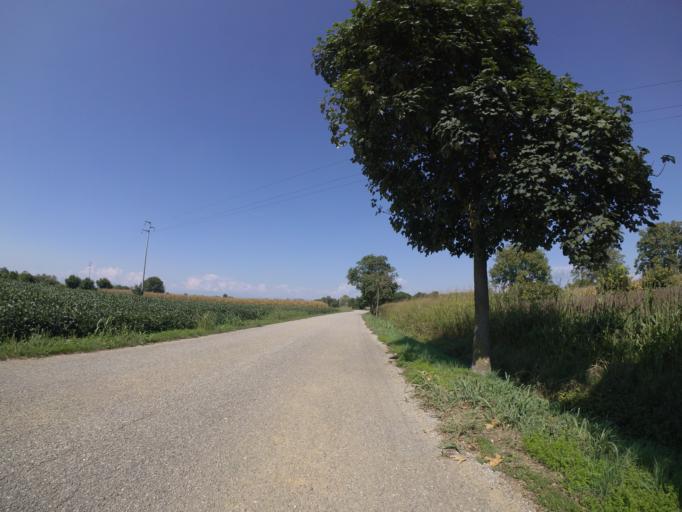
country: IT
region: Friuli Venezia Giulia
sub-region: Provincia di Udine
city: Bertiolo
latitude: 45.9410
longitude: 13.0897
